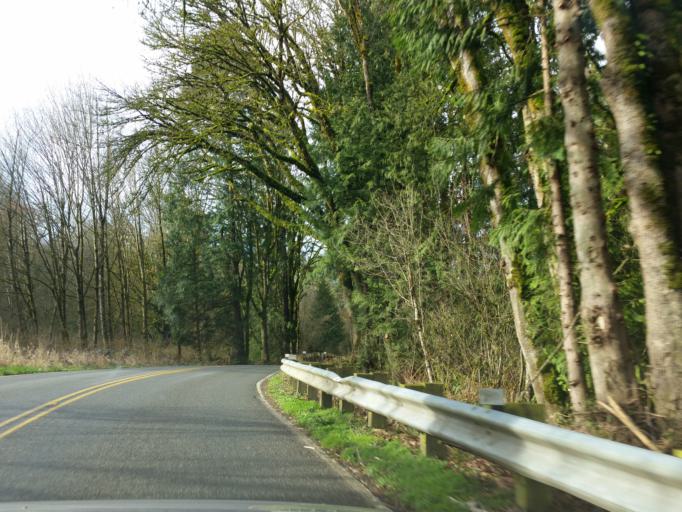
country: US
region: Washington
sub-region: Snohomish County
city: Cathcart
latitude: 47.8266
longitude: -122.0452
